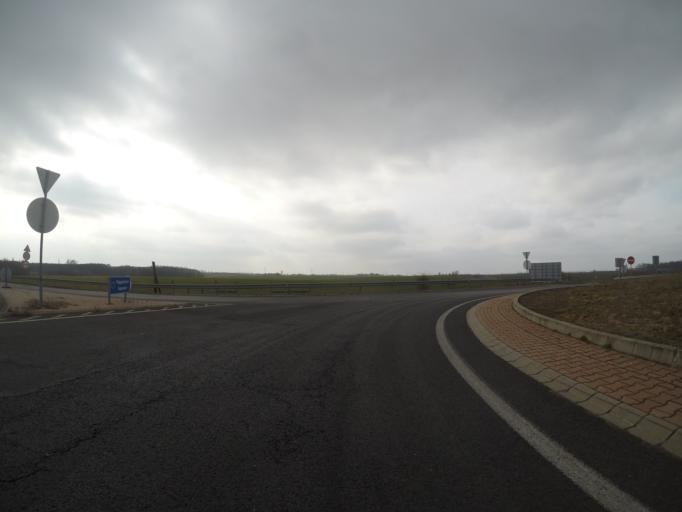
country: HU
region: Zala
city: Nagykanizsa
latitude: 46.4753
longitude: 17.0308
